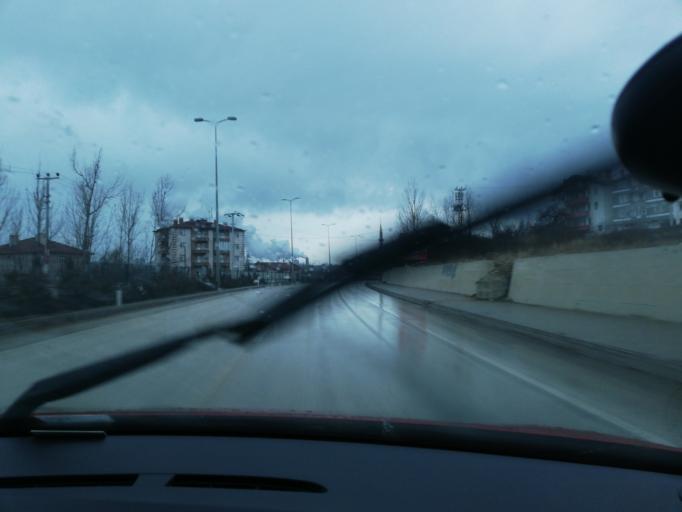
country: TR
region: Kastamonu
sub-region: Cide
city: Kastamonu
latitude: 41.4204
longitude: 33.8019
